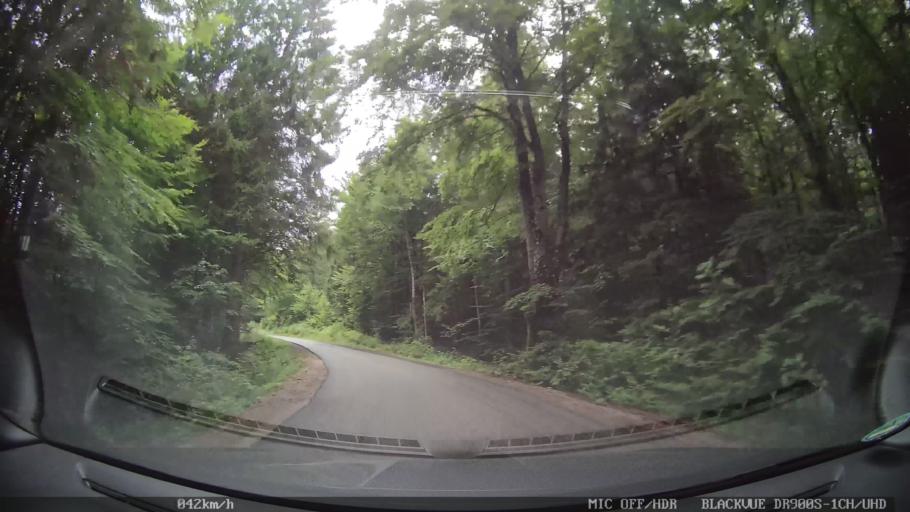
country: HR
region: Licko-Senjska
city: Jezerce
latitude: 44.9275
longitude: 15.5665
